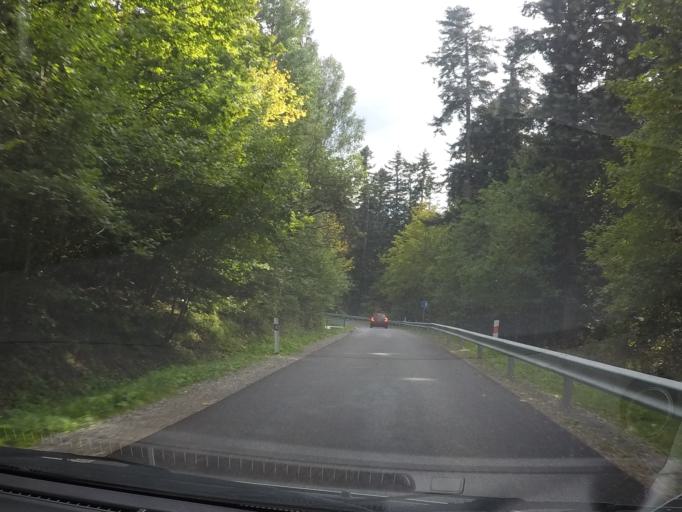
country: SK
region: Presovsky
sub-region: Okres Presov
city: Levoca
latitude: 49.0459
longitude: 20.6085
